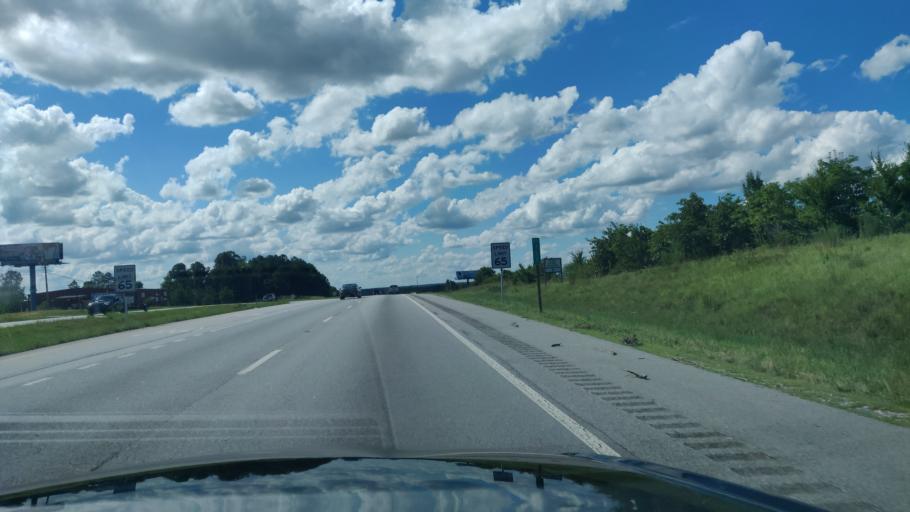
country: US
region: Alabama
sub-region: Russell County
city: Ladonia
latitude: 32.5107
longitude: -85.0579
